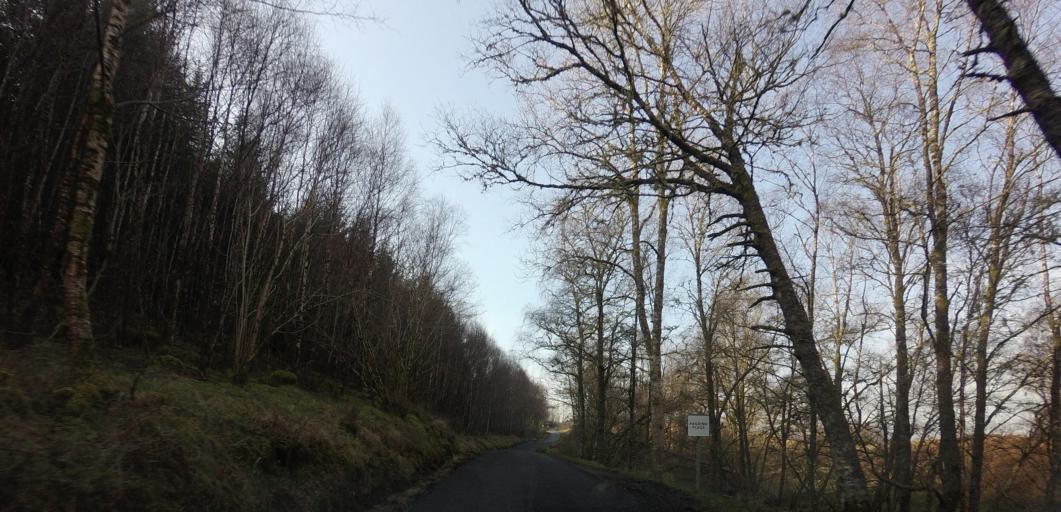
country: GB
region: Scotland
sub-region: Stirling
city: Callander
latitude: 56.4693
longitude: -4.2827
